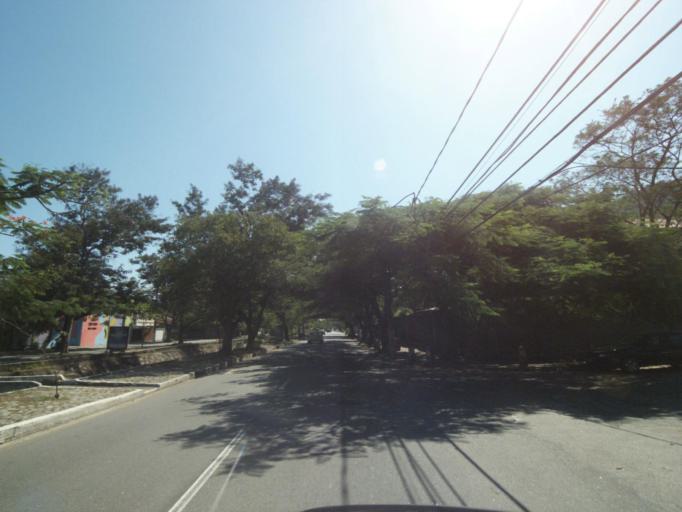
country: BR
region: Rio de Janeiro
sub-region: Niteroi
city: Niteroi
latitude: -22.9140
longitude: -43.0869
